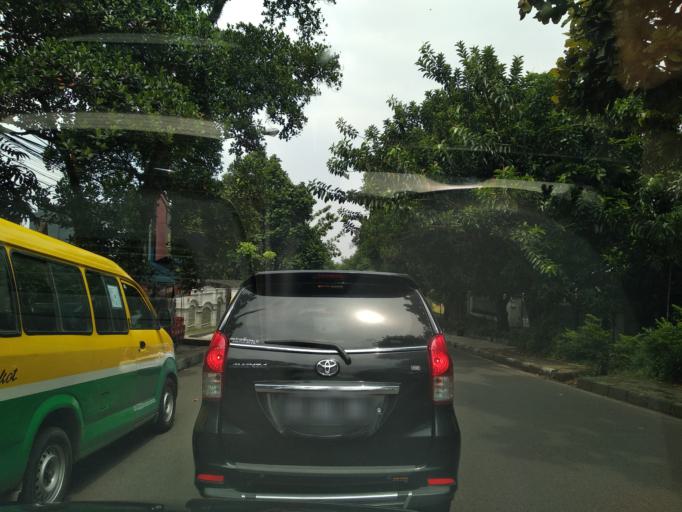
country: ID
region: West Java
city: Bandung
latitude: -6.8811
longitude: 107.5964
